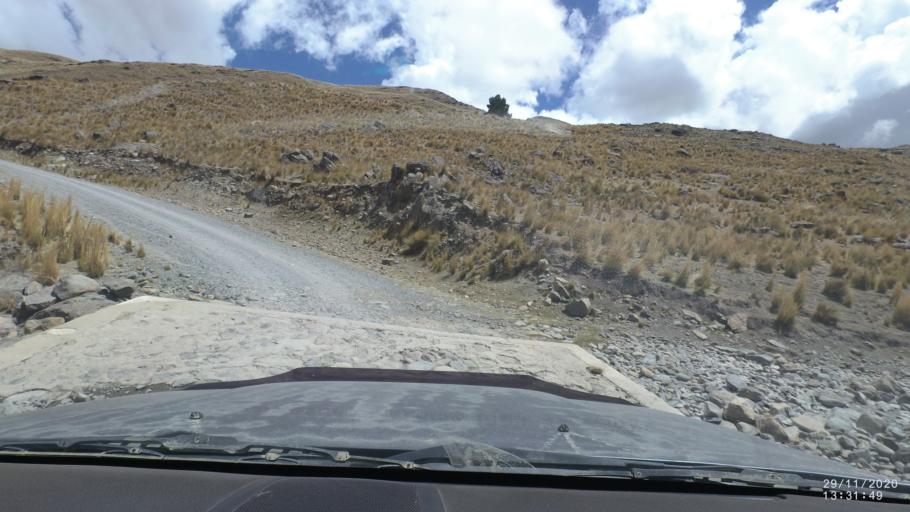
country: BO
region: Cochabamba
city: Cochabamba
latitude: -17.1070
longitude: -66.3446
